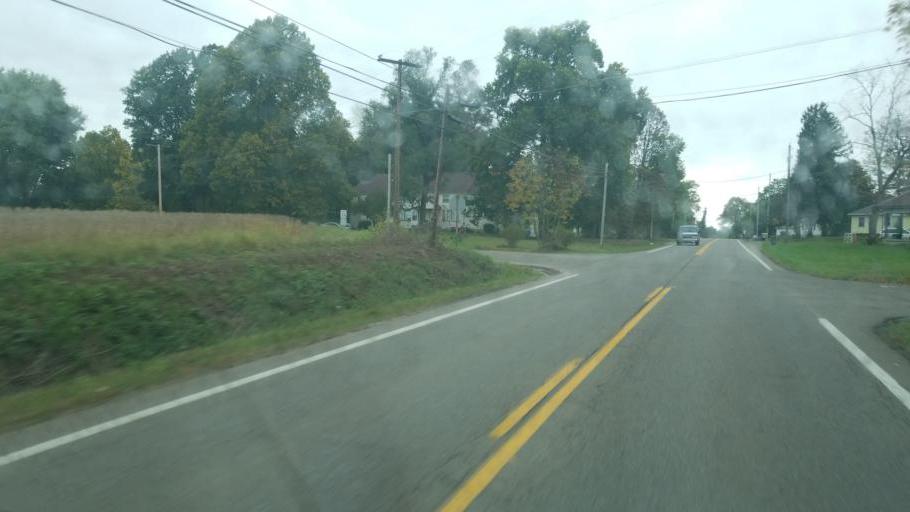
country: US
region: Ohio
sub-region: Richland County
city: Lincoln Heights
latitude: 40.7482
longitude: -82.4686
